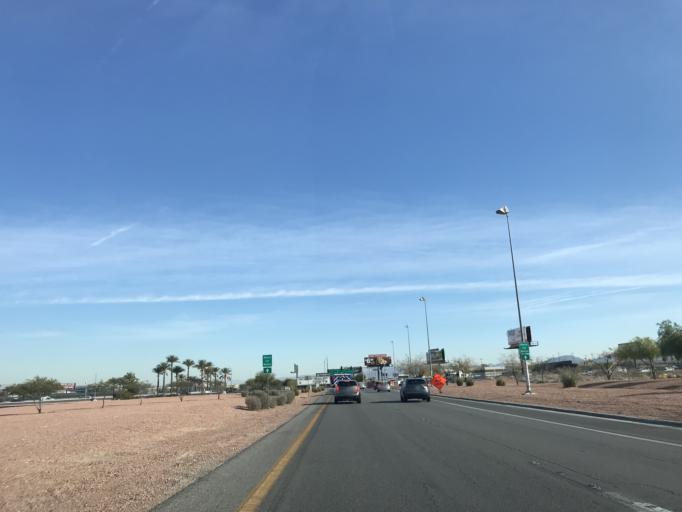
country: US
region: Nevada
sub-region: Clark County
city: Paradise
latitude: 36.0625
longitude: -115.1748
